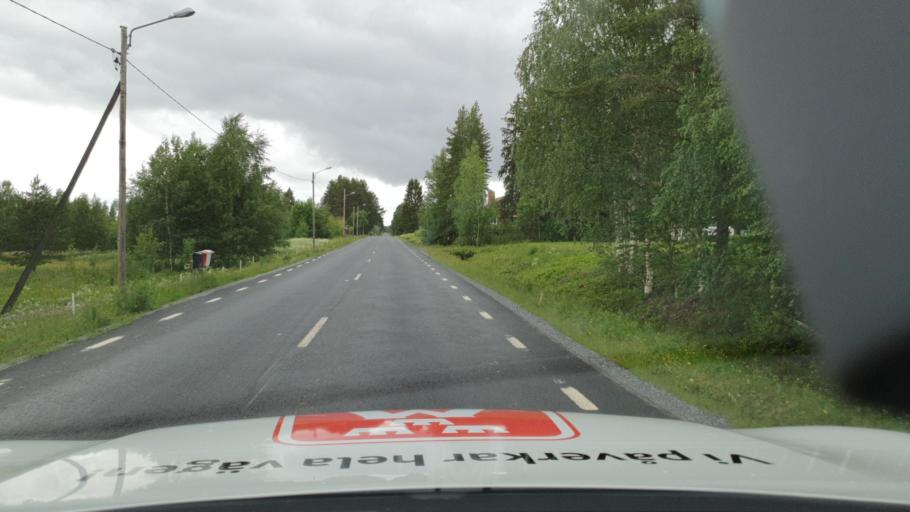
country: SE
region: Vaesterbotten
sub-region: Dorotea Kommun
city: Dorotea
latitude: 64.2221
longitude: 16.5451
